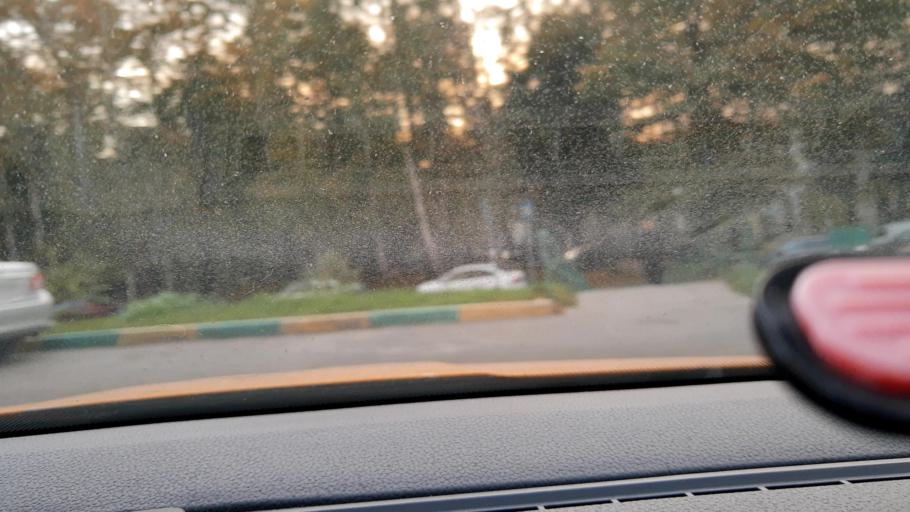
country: RU
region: Moskovskaya
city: Marfino
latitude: 55.7121
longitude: 37.3979
